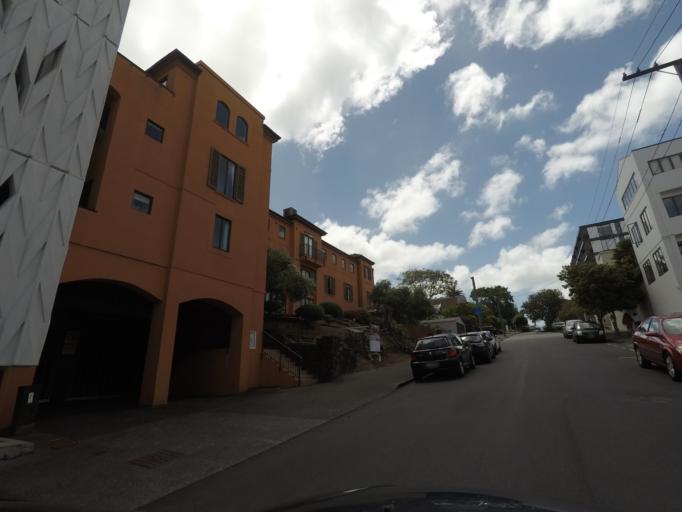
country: NZ
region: Auckland
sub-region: Auckland
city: Auckland
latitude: -36.8518
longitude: 174.7834
